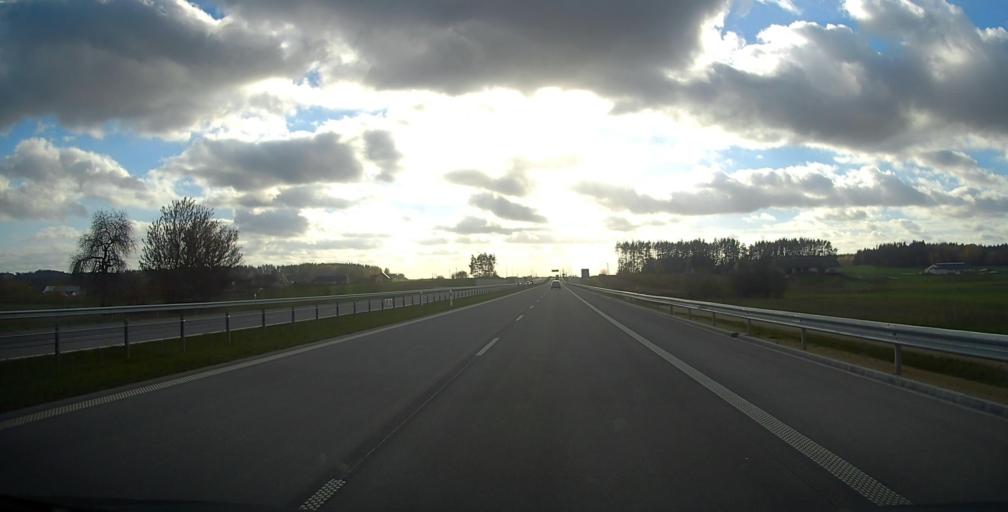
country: PL
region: Podlasie
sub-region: Powiat lomzynski
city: Piatnica
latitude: 53.2790
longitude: 22.1346
